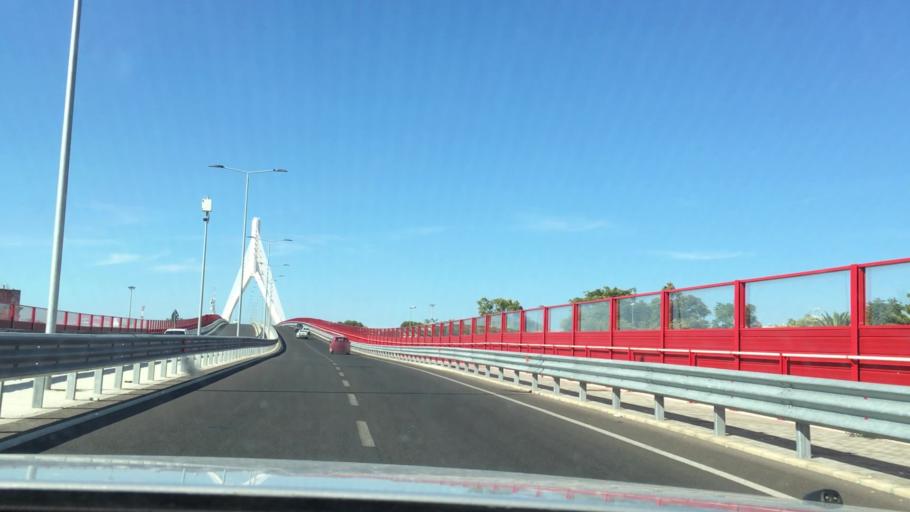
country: IT
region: Apulia
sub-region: Provincia di Bari
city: Bari
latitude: 41.1149
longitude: 16.8485
